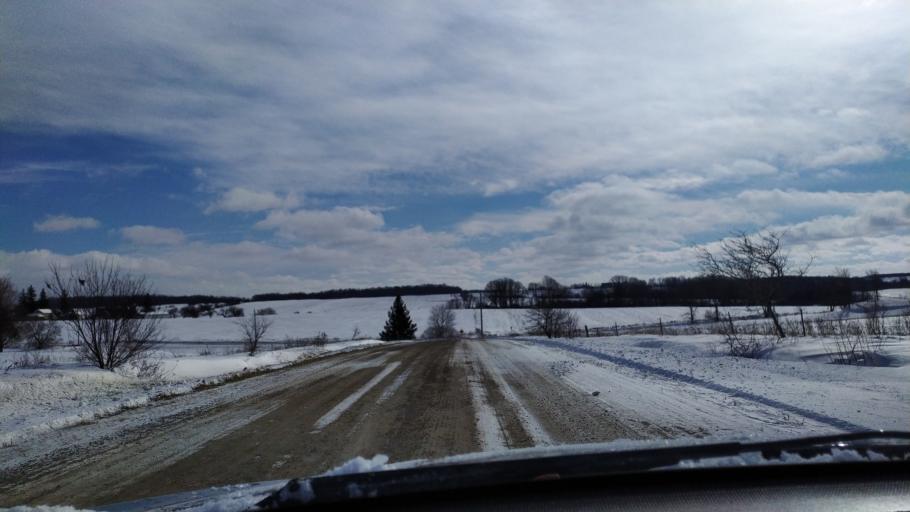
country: CA
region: Ontario
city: Waterloo
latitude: 43.4701
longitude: -80.7386
